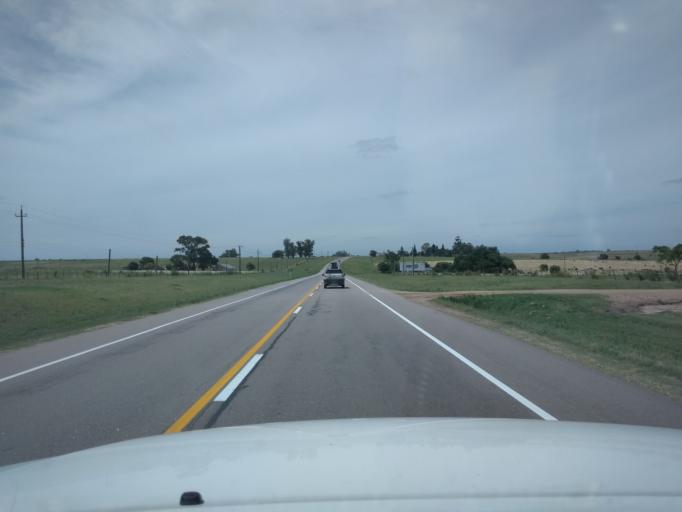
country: UY
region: Florida
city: Florida
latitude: -34.1742
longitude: -56.1892
